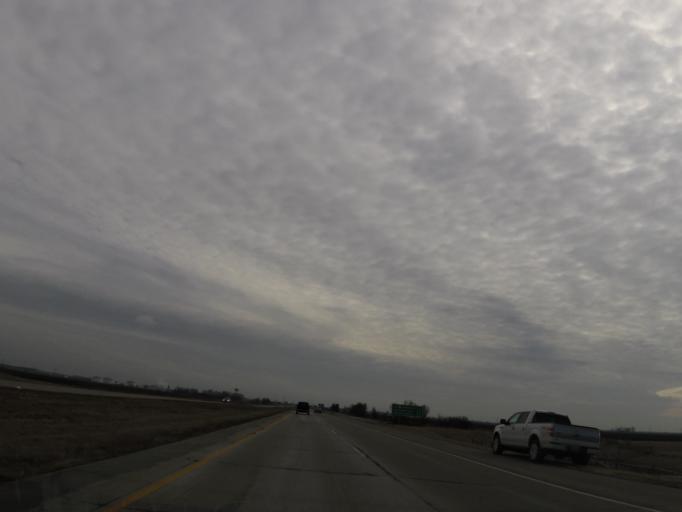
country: US
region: North Dakota
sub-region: Grand Forks County
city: Grand Forks
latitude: 47.9624
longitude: -97.0937
